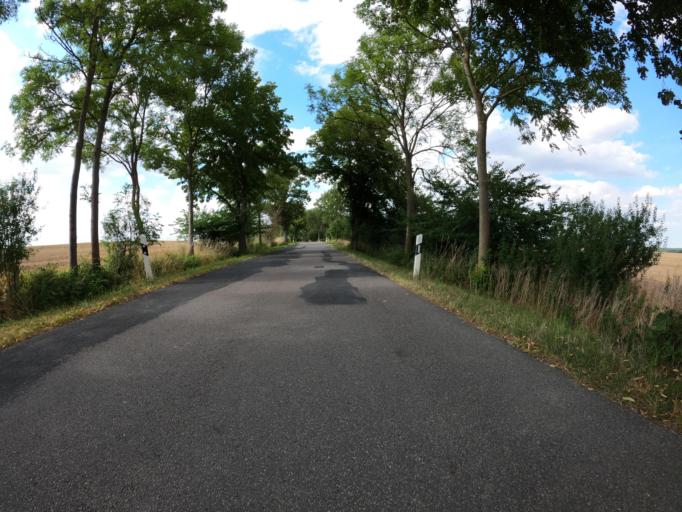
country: DE
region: Mecklenburg-Vorpommern
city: Woldegk
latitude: 53.4341
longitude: 13.6001
